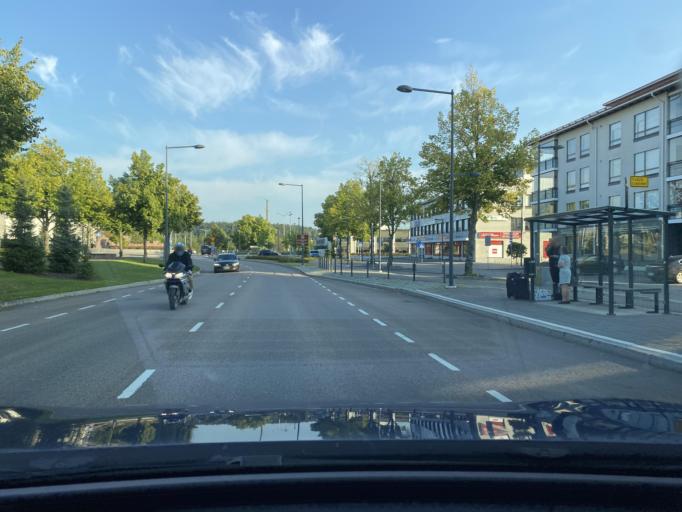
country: FI
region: Kymenlaakso
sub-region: Kouvola
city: Kouvola
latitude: 60.9070
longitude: 26.6236
